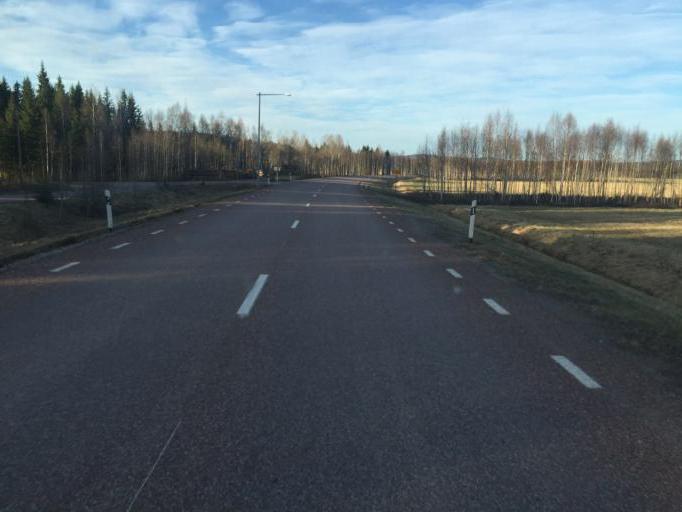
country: SE
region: Dalarna
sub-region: Gagnefs Kommun
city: Gagnef
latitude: 60.5420
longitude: 15.0600
